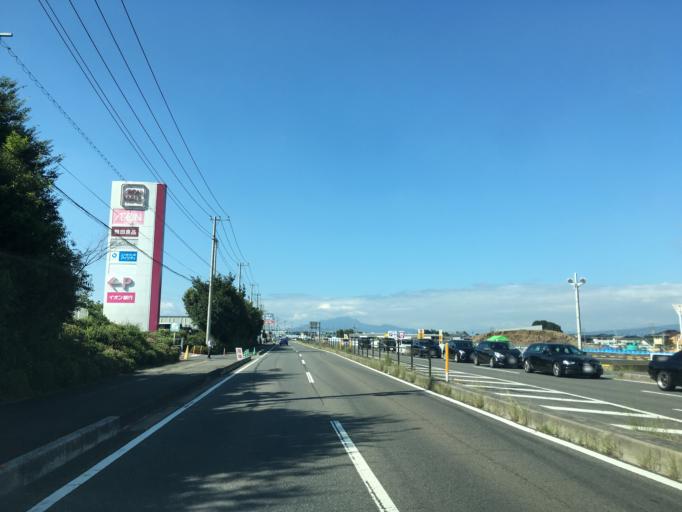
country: JP
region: Gunma
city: Kanekomachi
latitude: 36.3895
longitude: 139.0084
